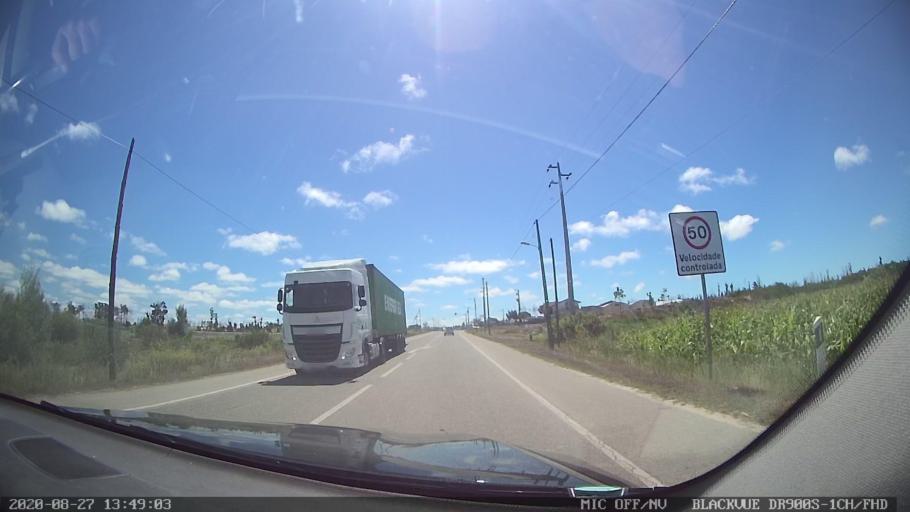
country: PT
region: Coimbra
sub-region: Mira
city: Mira
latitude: 40.3710
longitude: -8.7458
